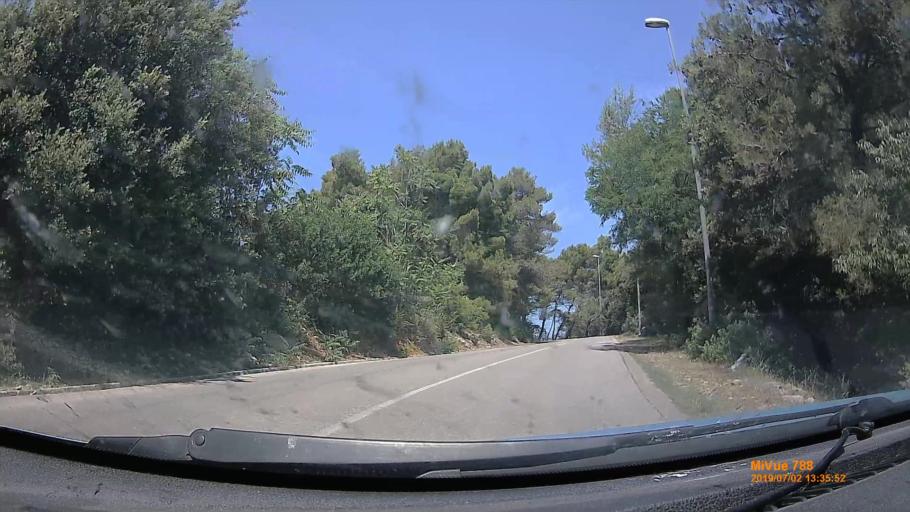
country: HR
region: Primorsko-Goranska
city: Mali Losinj
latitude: 44.5199
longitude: 14.4973
